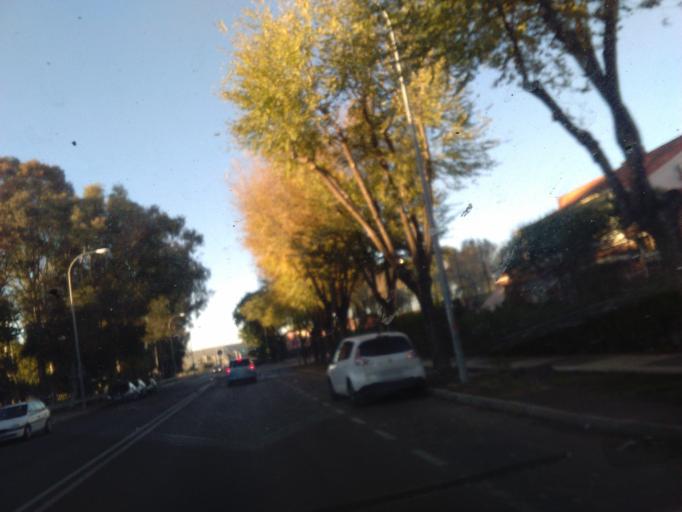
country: ES
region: Andalusia
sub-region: Provincia de Sevilla
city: Sevilla
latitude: 37.3988
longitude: -5.9312
